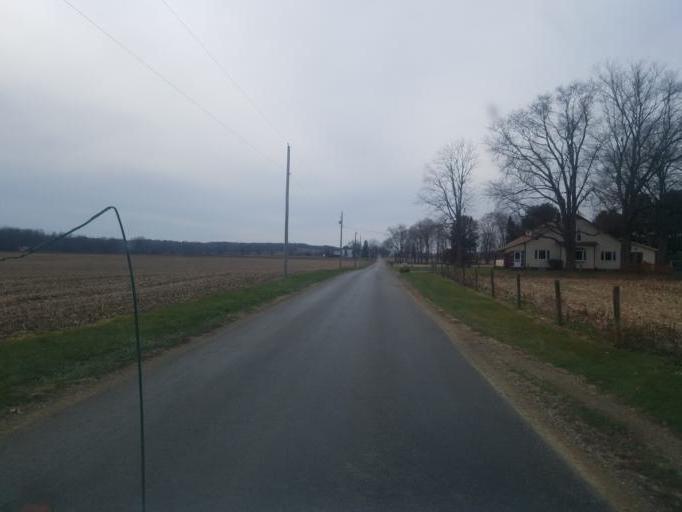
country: US
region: Ohio
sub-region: Knox County
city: Mount Vernon
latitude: 40.4189
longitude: -82.5152
